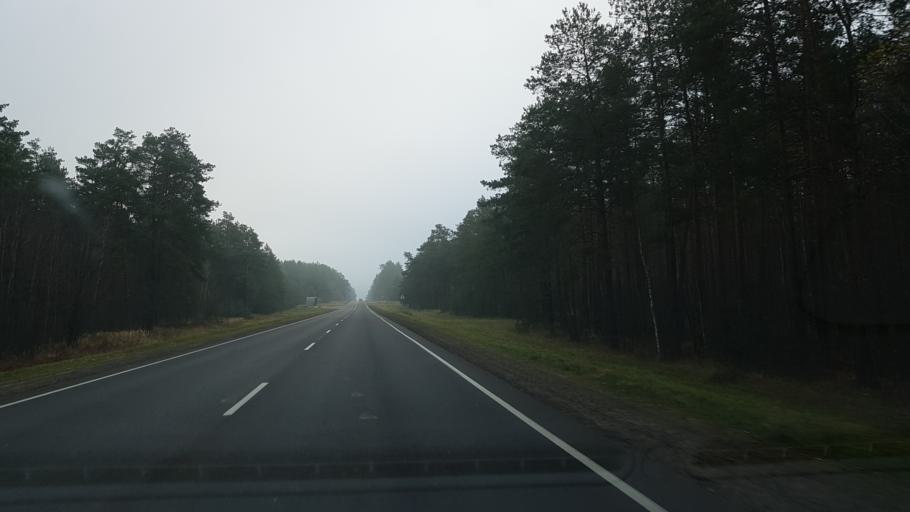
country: BY
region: Mogilev
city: Babruysk
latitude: 53.1596
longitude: 29.3212
